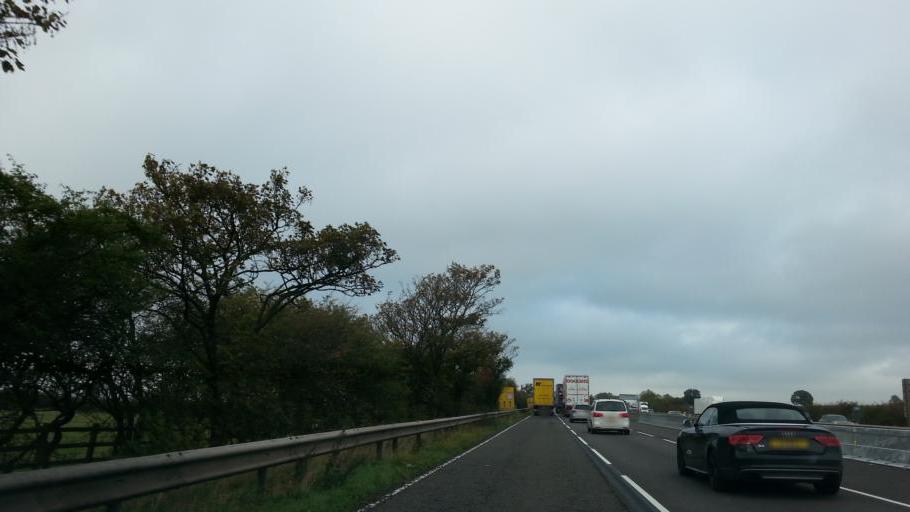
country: GB
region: England
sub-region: Staffordshire
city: Stafford
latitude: 52.8379
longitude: -2.1502
